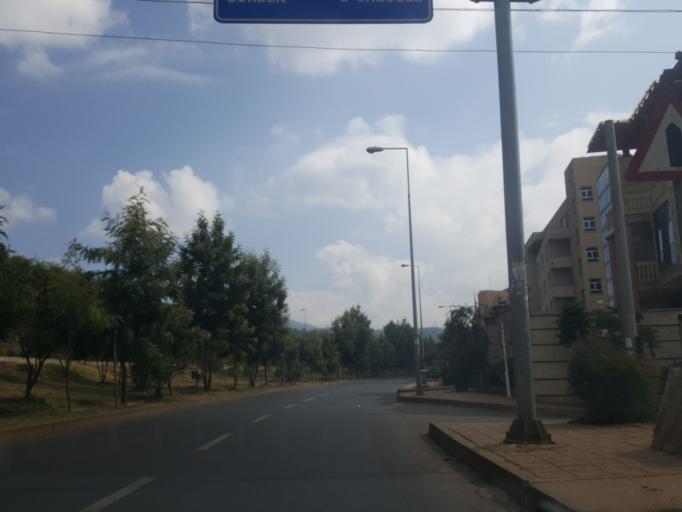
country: ET
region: Adis Abeba
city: Addis Ababa
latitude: 9.0689
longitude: 38.7177
